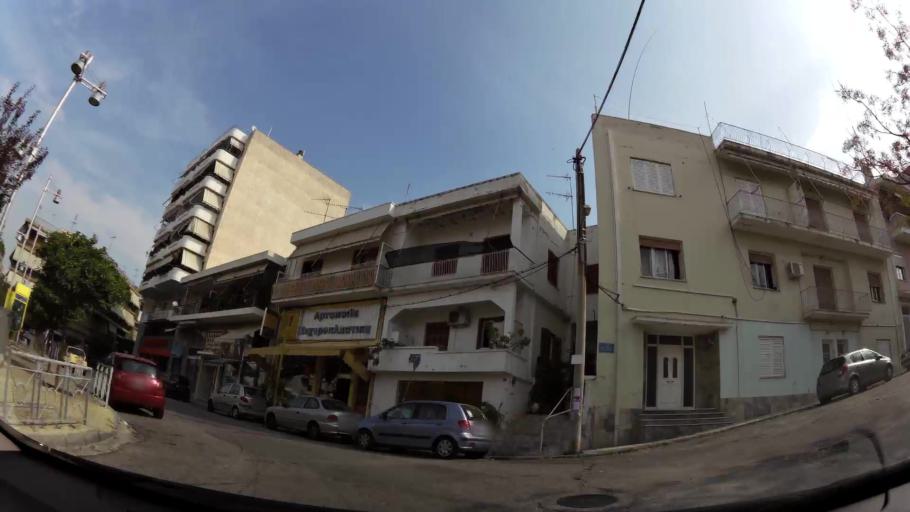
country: GR
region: Attica
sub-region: Nomarchia Athinas
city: Galatsi
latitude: 38.0154
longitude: 23.7584
